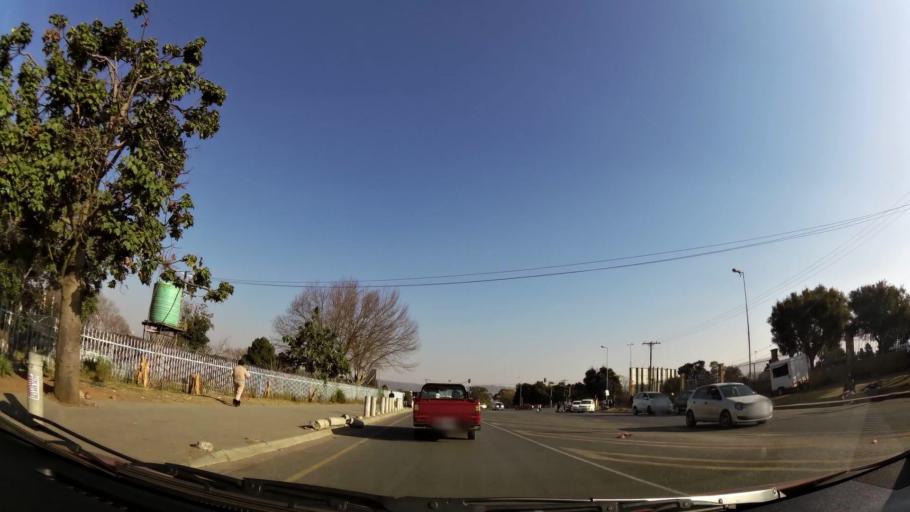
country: ZA
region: Gauteng
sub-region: West Rand District Municipality
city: Muldersdriseloop
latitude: -26.0595
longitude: 27.9020
